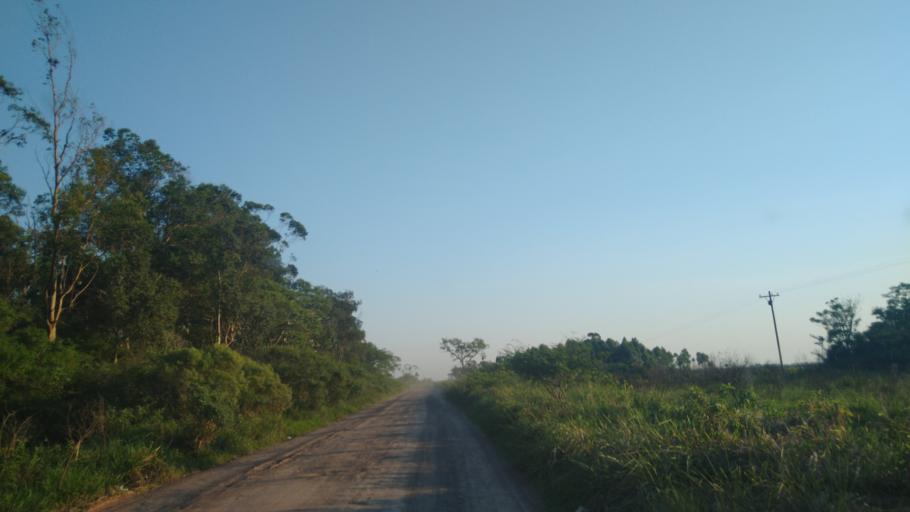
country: PY
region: Neembucu
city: Cerrito
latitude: -27.3979
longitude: -57.6585
